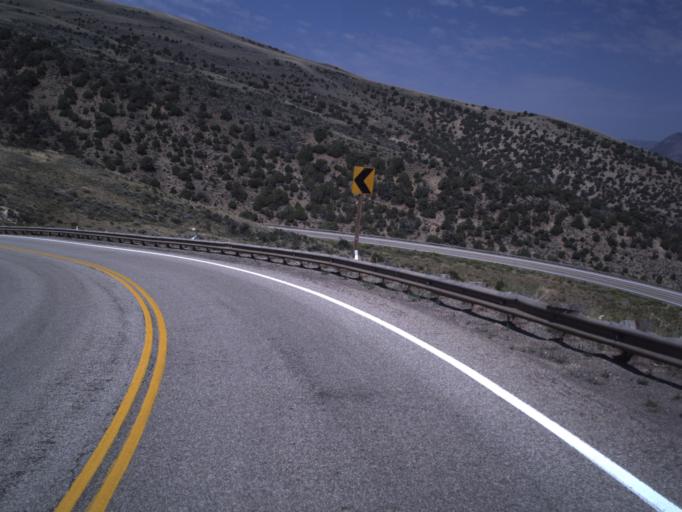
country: US
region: Utah
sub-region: Daggett County
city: Manila
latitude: 40.9087
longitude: -109.6983
